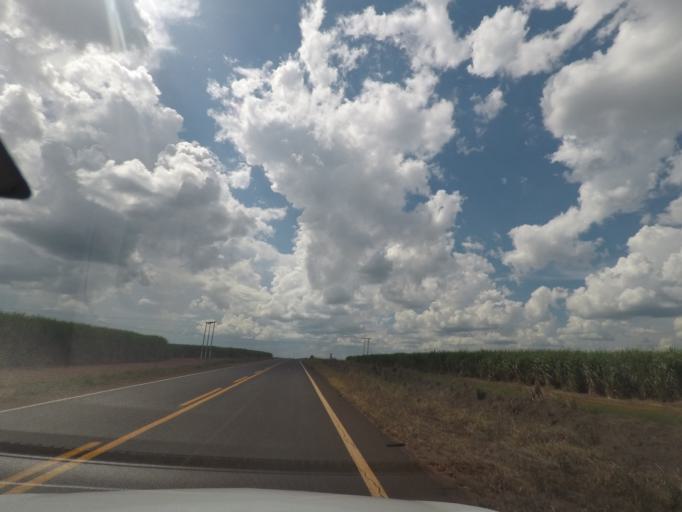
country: BR
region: Minas Gerais
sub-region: Conceicao Das Alagoas
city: Conceicao das Alagoas
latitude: -19.8305
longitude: -48.5909
